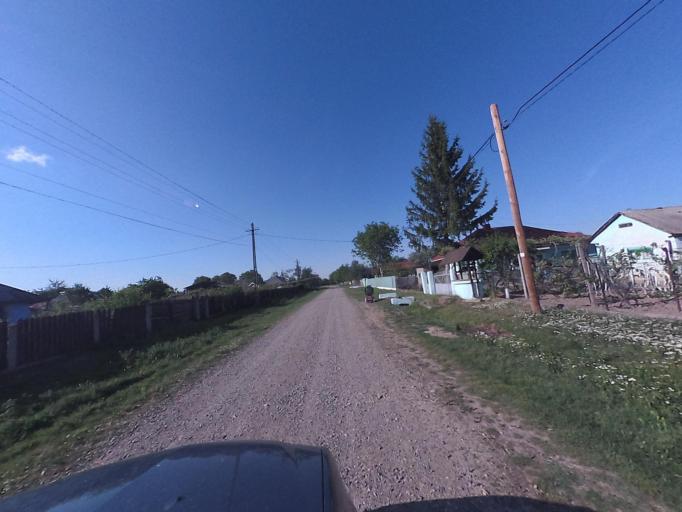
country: RO
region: Neamt
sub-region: Comuna Cordun
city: Pildesti
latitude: 46.9784
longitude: 26.8116
